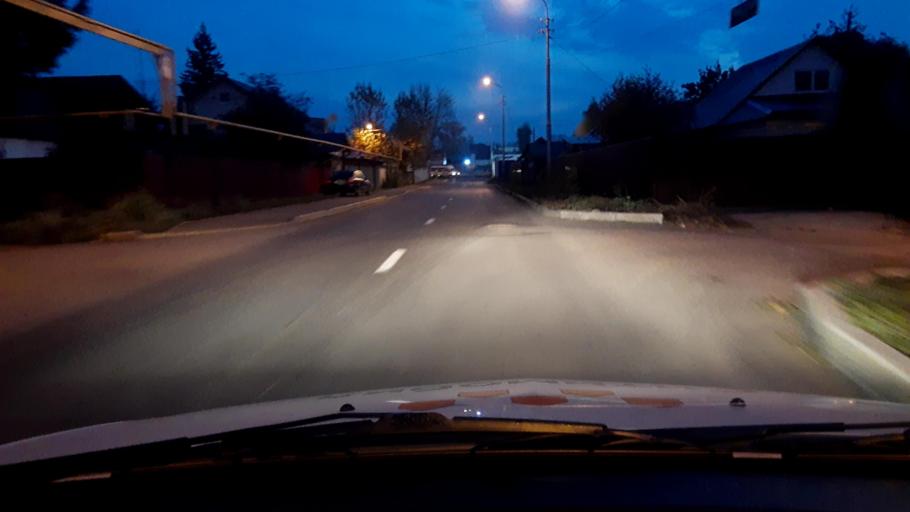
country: RU
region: Bashkortostan
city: Ufa
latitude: 54.8223
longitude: 56.0995
